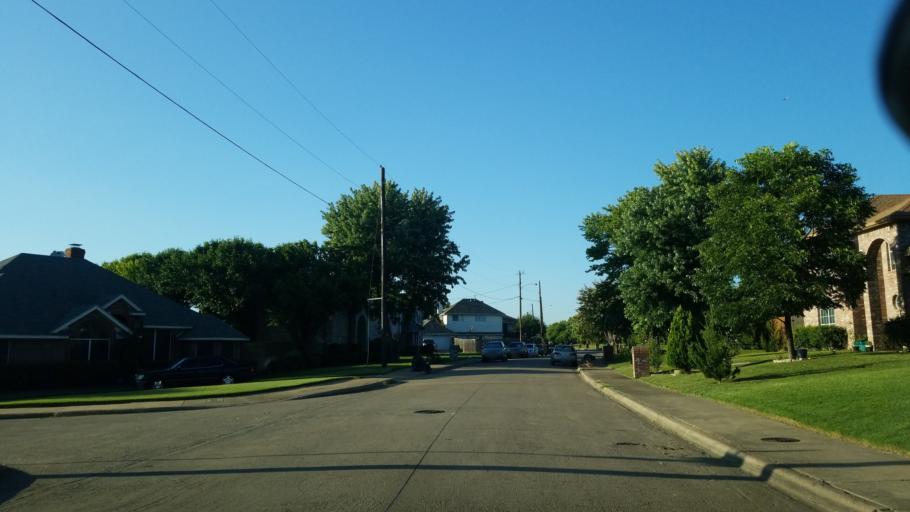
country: US
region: Texas
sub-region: Dallas County
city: Balch Springs
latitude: 32.7791
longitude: -96.6962
